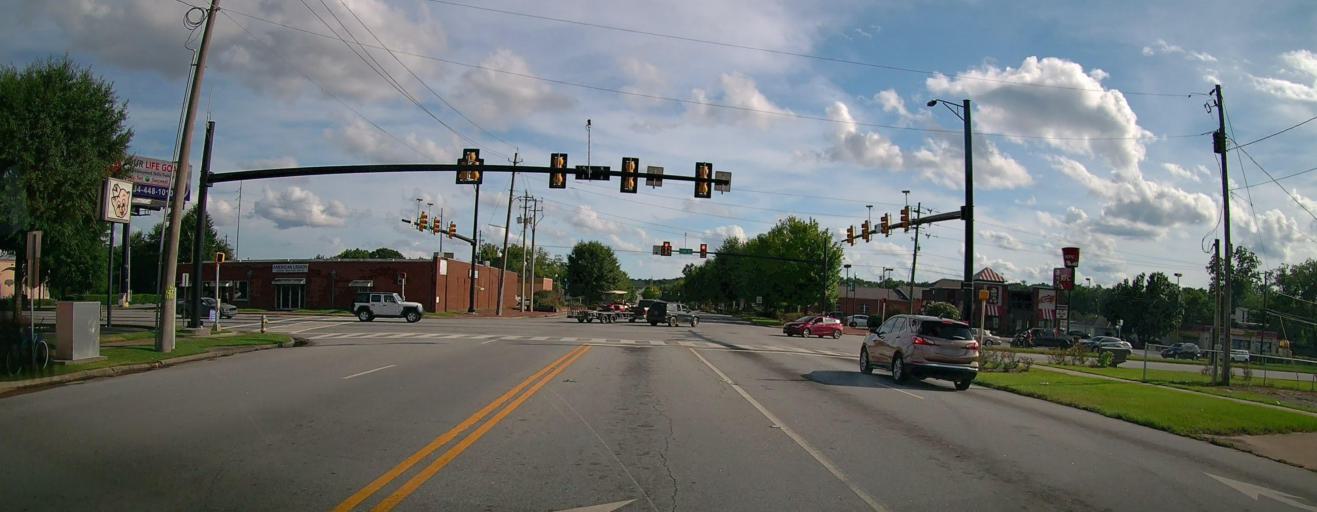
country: US
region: Alabama
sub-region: Russell County
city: Phenix City
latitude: 32.4717
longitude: -85.0007
